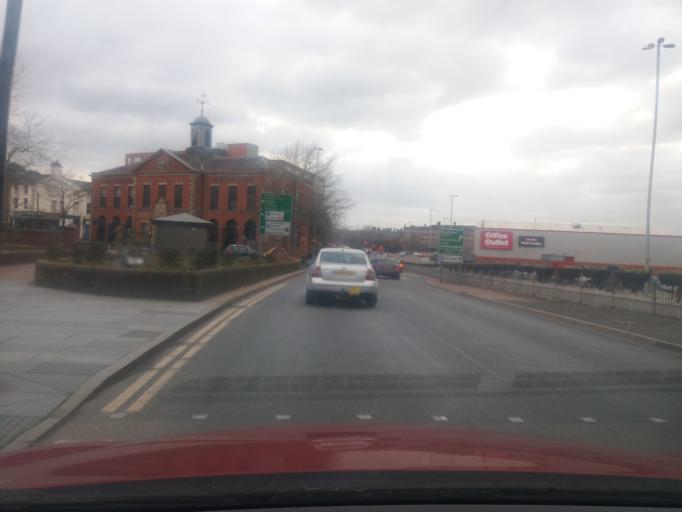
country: GB
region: England
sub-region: Lancashire
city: Preston
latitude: 53.7599
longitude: -2.7029
